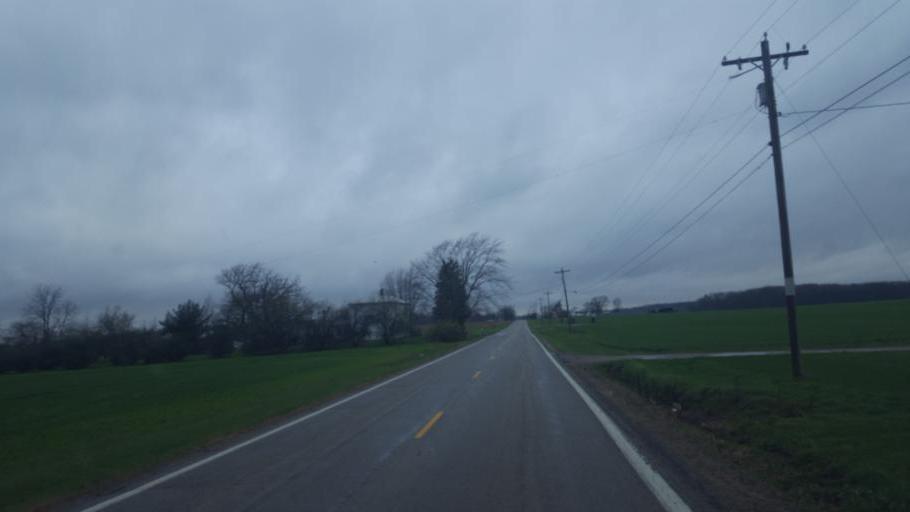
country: US
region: Ohio
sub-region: Morrow County
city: Cardington
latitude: 40.4846
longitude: -82.8509
